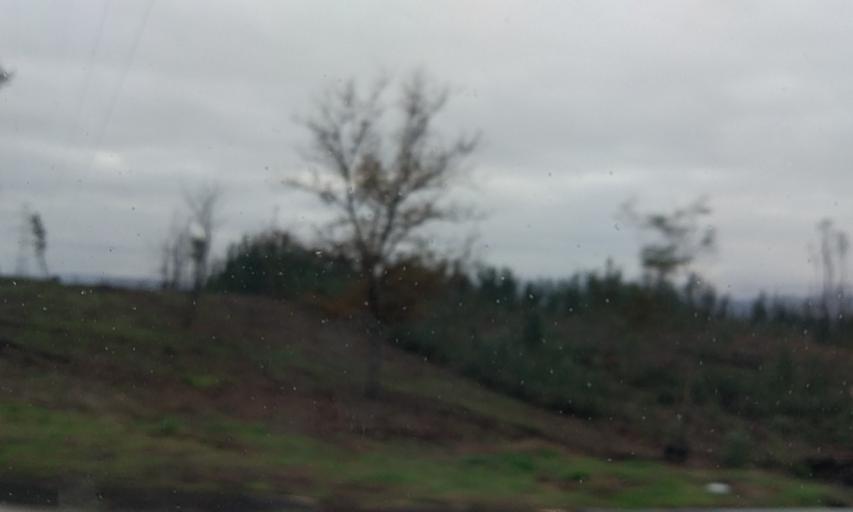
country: PT
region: Viseu
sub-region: Mortagua
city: Mortagua
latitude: 40.3637
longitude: -8.1943
